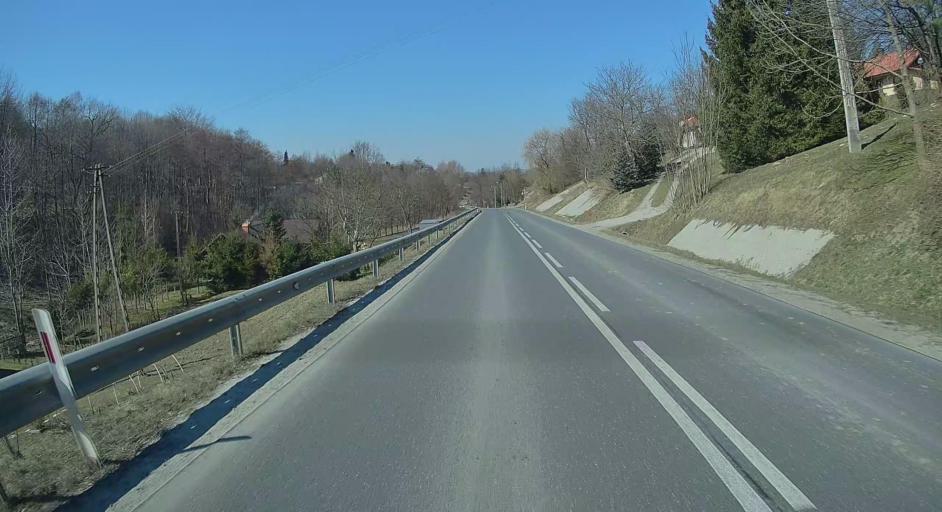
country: PL
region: Subcarpathian Voivodeship
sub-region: Powiat rzeszowski
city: Hyzne
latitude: 49.9012
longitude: 22.2138
